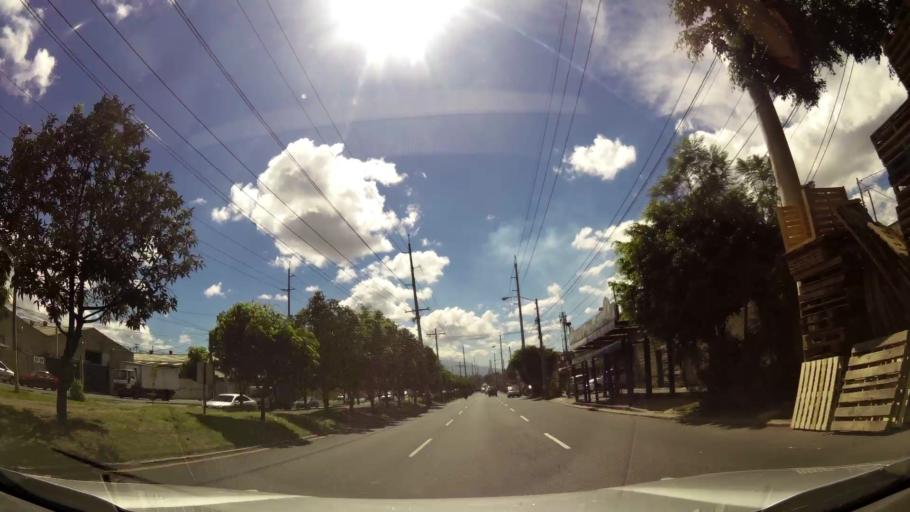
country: GT
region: Guatemala
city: Santa Catarina Pinula
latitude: 14.5656
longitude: -90.5450
